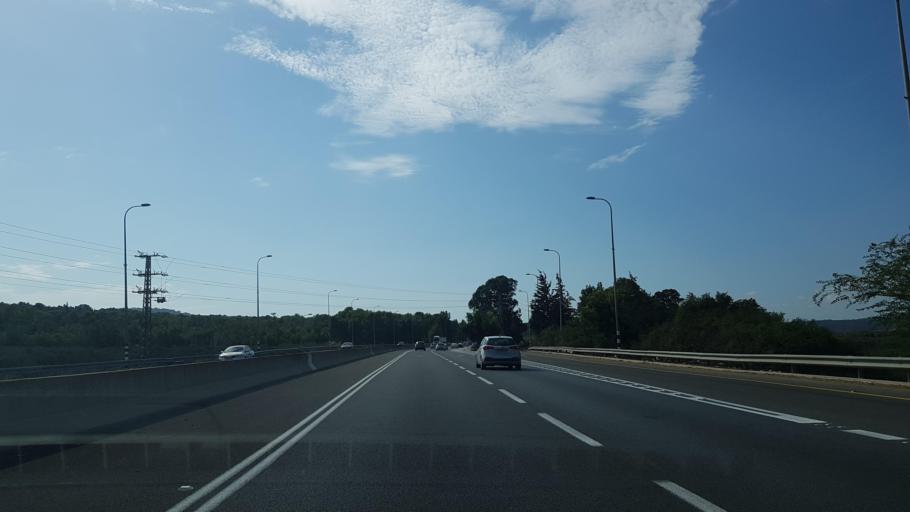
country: IL
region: Northern District
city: Kafr Kanna
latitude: 32.7603
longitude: 35.3592
